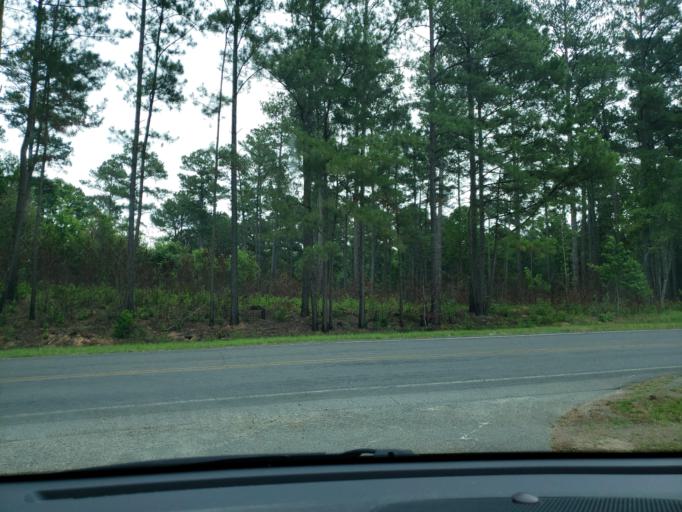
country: US
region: North Carolina
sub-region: Chatham County
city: Fearrington Village
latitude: 35.6928
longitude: -79.0150
